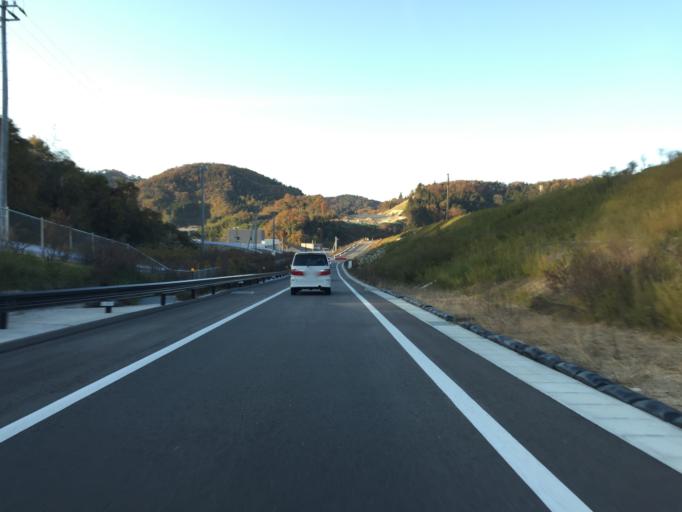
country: JP
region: Fukushima
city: Hobaramachi
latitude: 37.7639
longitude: 140.5914
